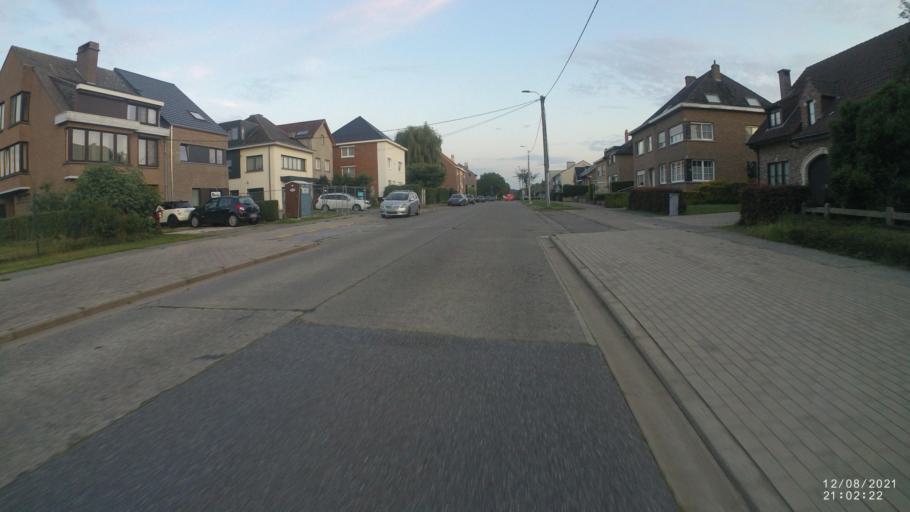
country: BE
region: Flanders
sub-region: Provincie Vlaams-Brabant
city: Dilbeek
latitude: 50.8637
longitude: 4.2455
